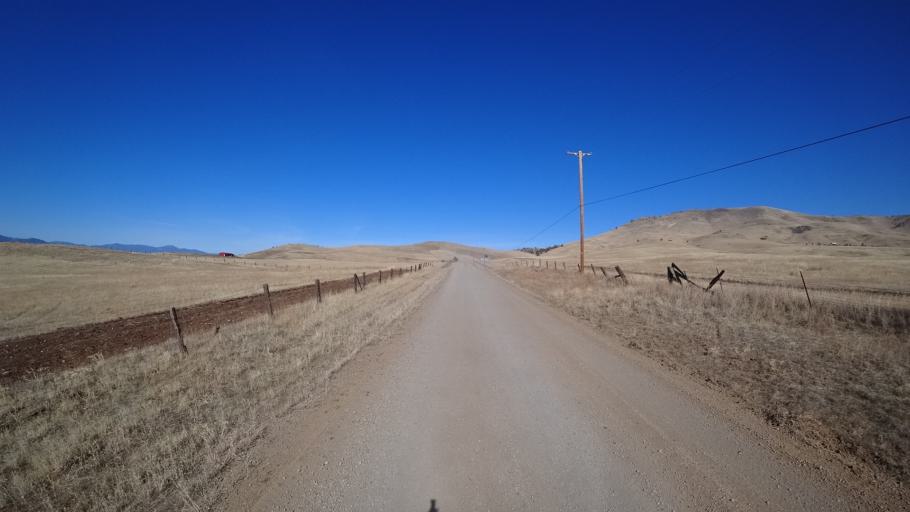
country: US
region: California
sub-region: Siskiyou County
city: Montague
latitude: 41.8376
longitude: -122.4206
